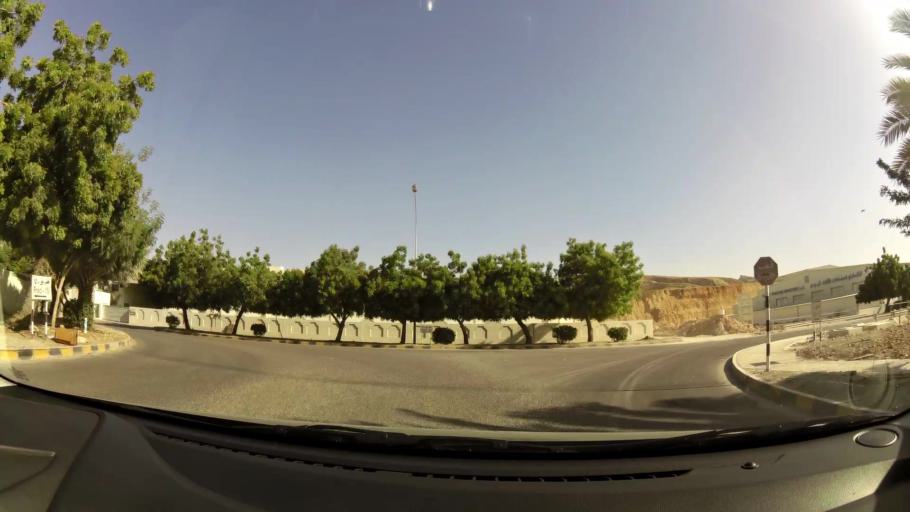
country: OM
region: Muhafazat Masqat
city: As Sib al Jadidah
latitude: 23.5522
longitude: 58.2231
